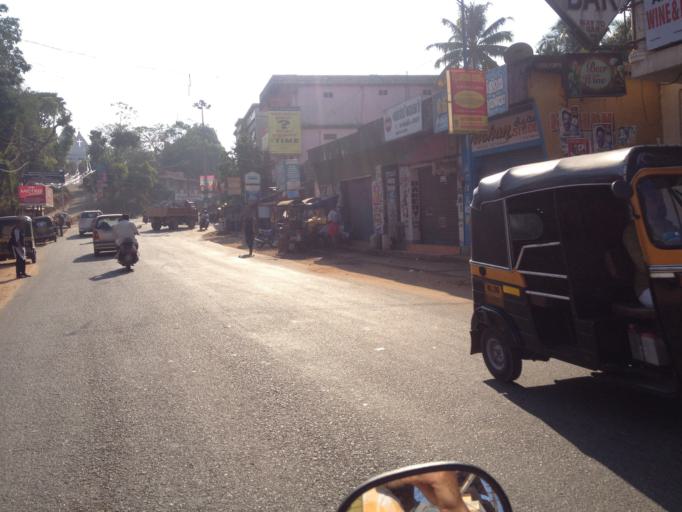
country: IN
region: Kerala
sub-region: Kollam
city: Punalur
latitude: 9.0053
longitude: 76.7850
